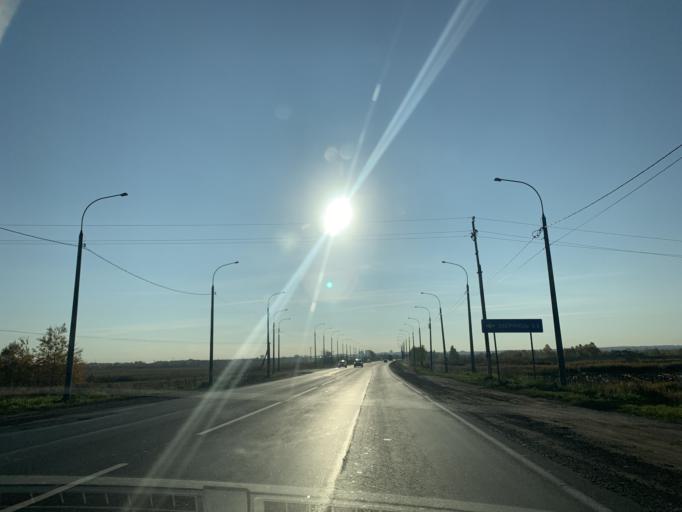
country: RU
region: Jaroslavl
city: Yaroslavl
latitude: 57.6270
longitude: 39.7612
